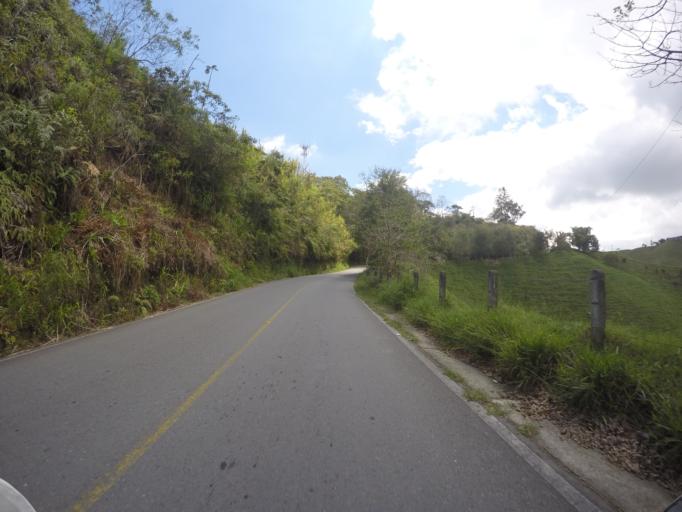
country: CO
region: Quindio
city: Filandia
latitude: 4.6567
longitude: -75.6732
